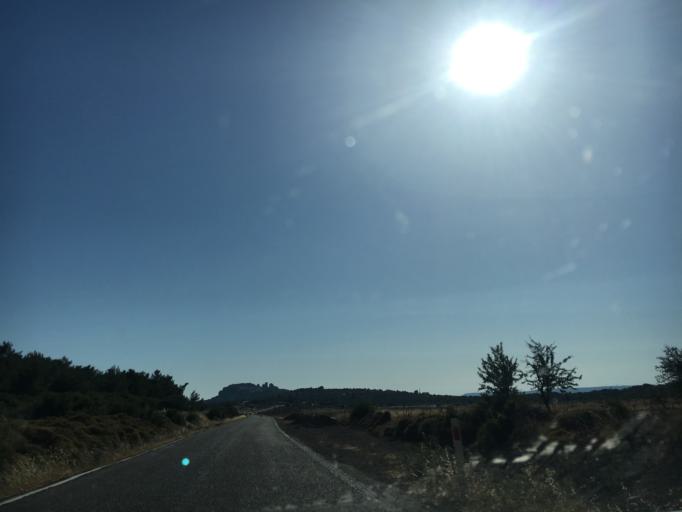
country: TR
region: Canakkale
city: Behram
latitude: 39.4996
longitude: 26.3627
